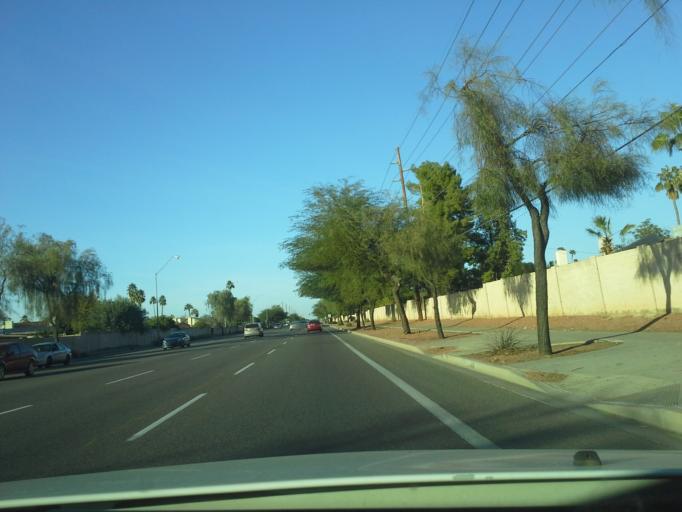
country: US
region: Arizona
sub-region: Maricopa County
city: Glendale
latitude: 33.6435
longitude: -112.1344
